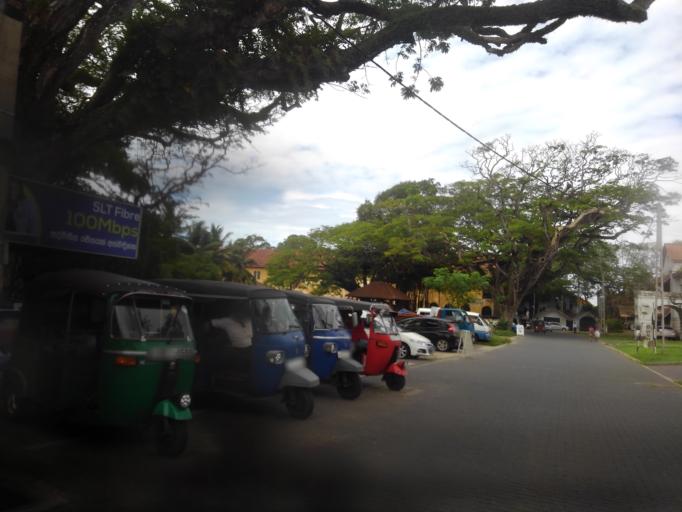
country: LK
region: Southern
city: Galle
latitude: 6.0273
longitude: 80.2194
